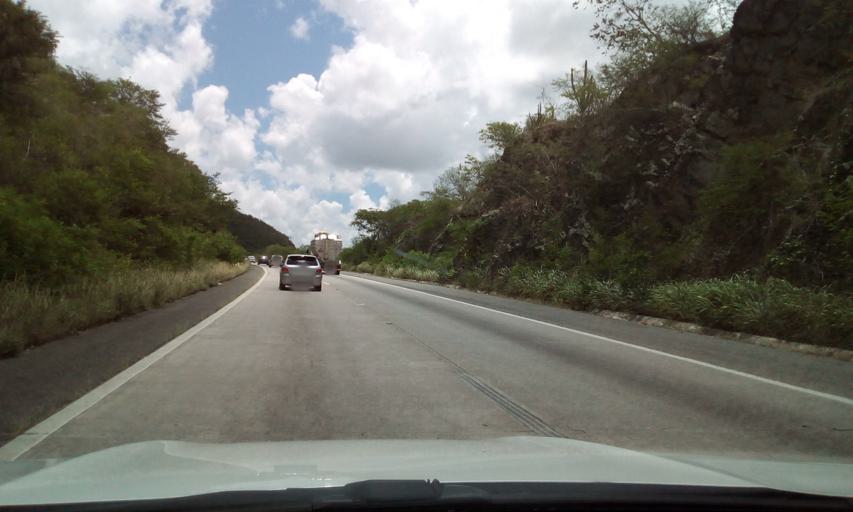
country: BR
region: Pernambuco
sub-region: Cha Grande
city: Cha Grande
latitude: -8.1673
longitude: -35.4666
